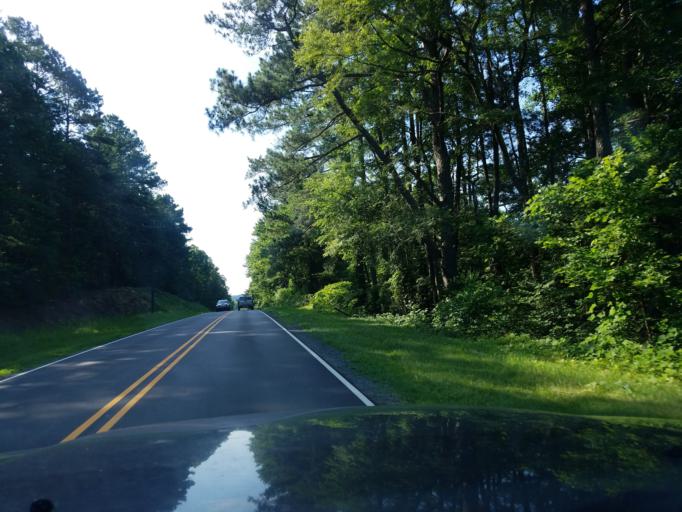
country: US
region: North Carolina
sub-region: Granville County
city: Butner
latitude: 36.1620
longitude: -78.7795
